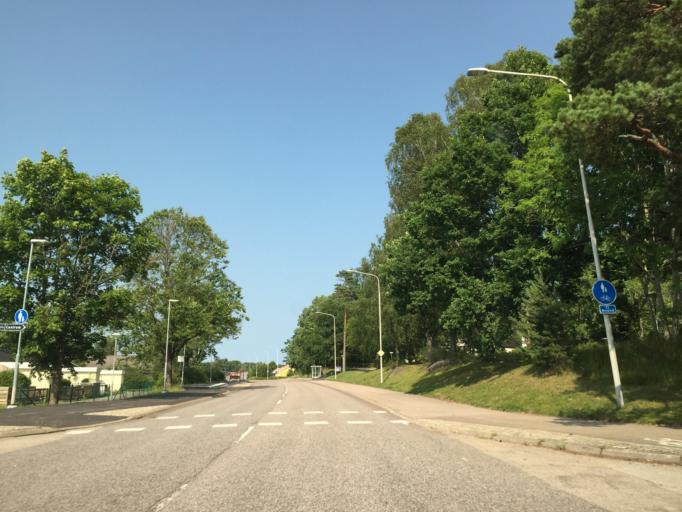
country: SE
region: Vaestra Goetaland
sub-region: Vanersborgs Kommun
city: Vanersborg
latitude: 58.3749
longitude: 12.2906
